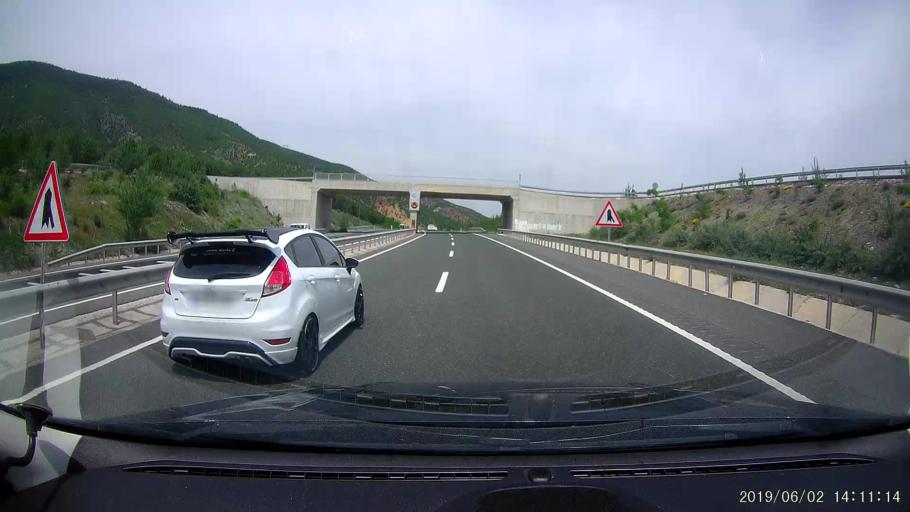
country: TR
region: Cankiri
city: Yaprakli
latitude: 40.9068
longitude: 33.7803
